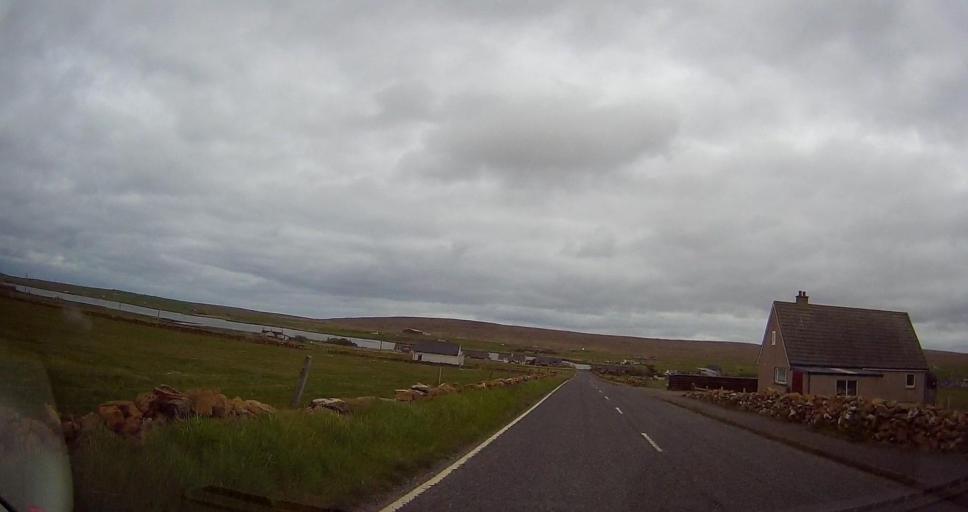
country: GB
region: Scotland
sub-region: Shetland Islands
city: Shetland
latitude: 60.7625
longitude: -0.8589
